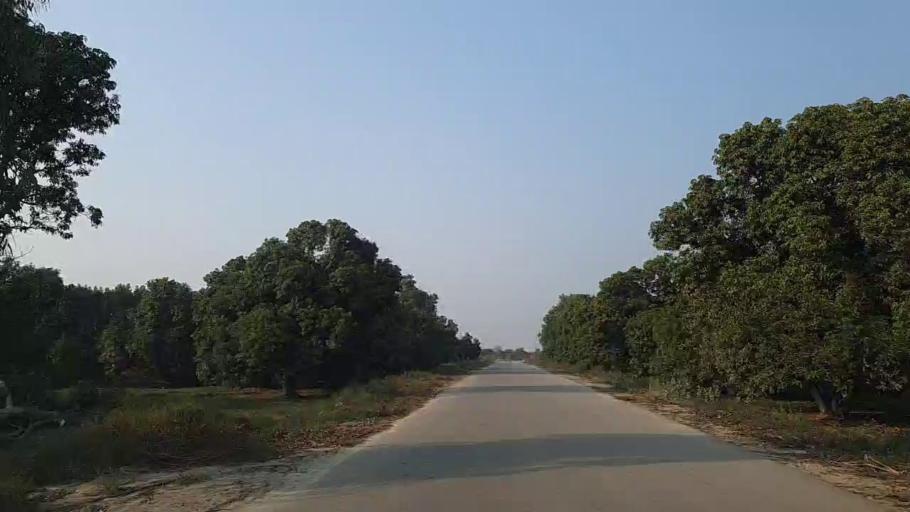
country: PK
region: Sindh
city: Sann
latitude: 26.1092
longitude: 68.1504
